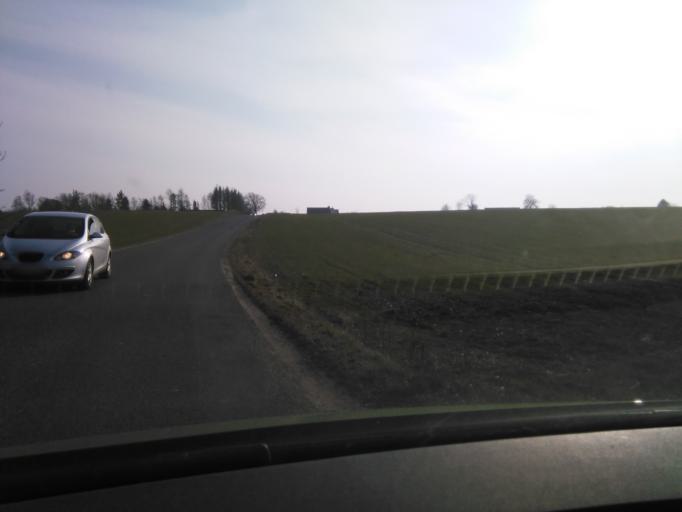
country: DK
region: Central Jutland
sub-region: Arhus Kommune
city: Marslet
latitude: 56.0792
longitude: 10.1658
